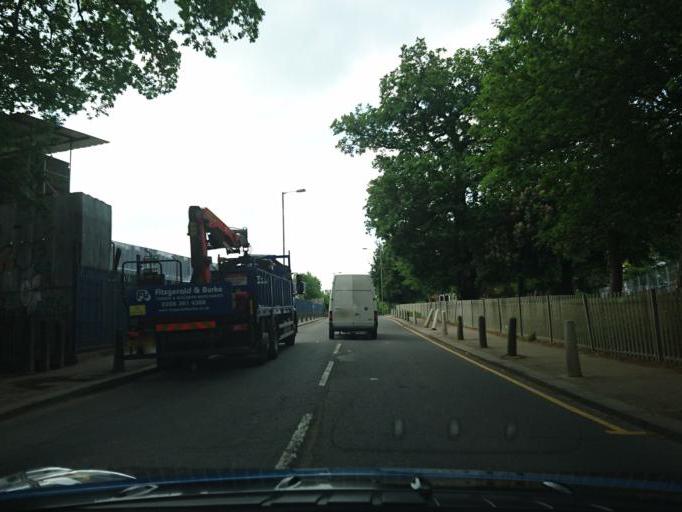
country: GB
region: England
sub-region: Greater London
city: Wood Green
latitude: 51.6209
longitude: -0.1483
